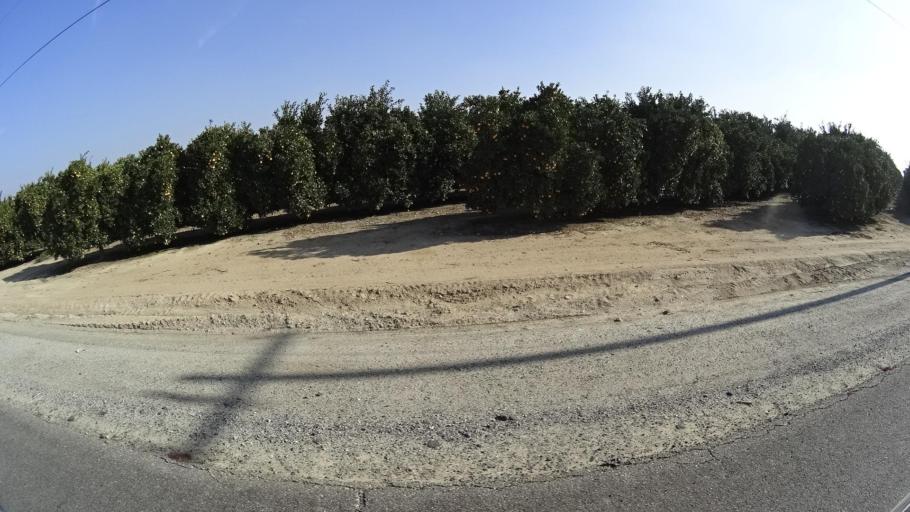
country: US
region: California
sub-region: Kern County
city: McFarland
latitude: 35.6698
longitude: -119.1893
